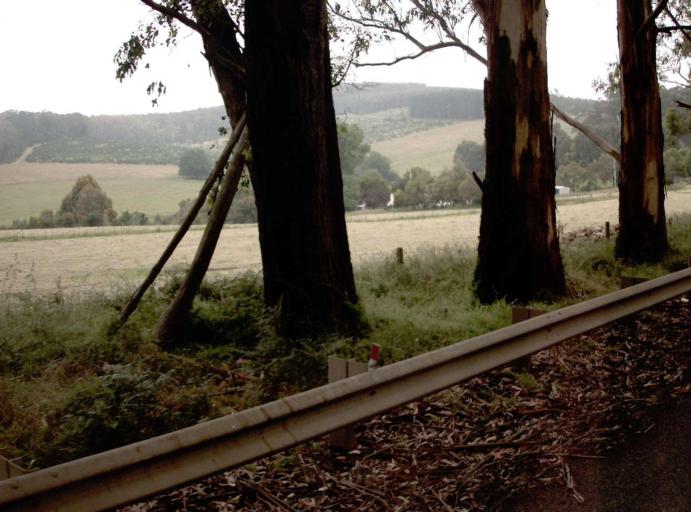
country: AU
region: Victoria
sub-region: Latrobe
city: Moe
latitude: -38.3323
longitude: 146.2310
